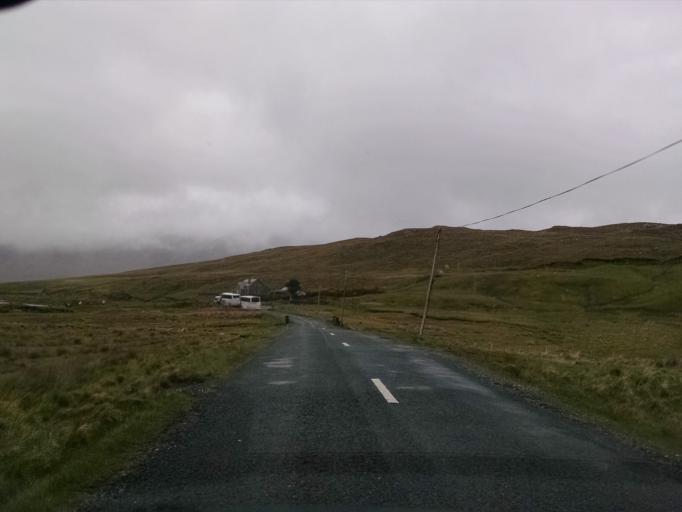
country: IE
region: Connaught
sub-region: County Galway
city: Clifden
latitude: 53.4946
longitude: -9.7365
